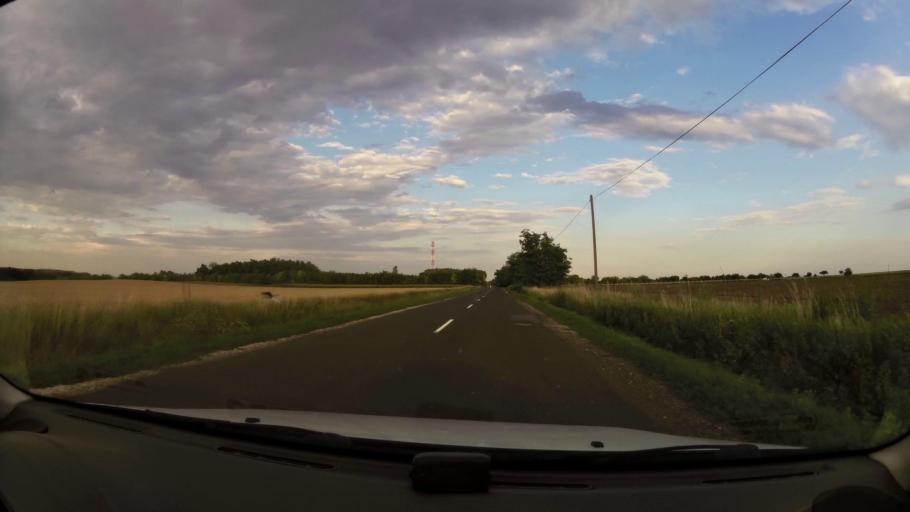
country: HU
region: Pest
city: Tapioszentmarton
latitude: 47.3475
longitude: 19.7183
